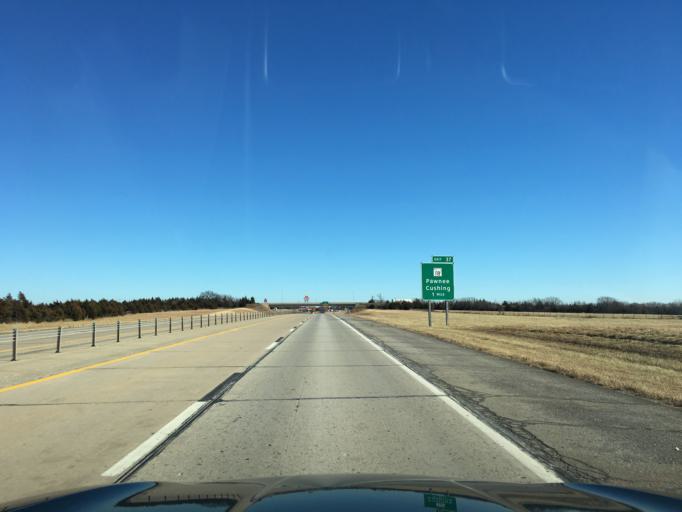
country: US
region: Oklahoma
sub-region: Pawnee County
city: Pawnee
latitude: 36.2247
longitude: -96.8071
